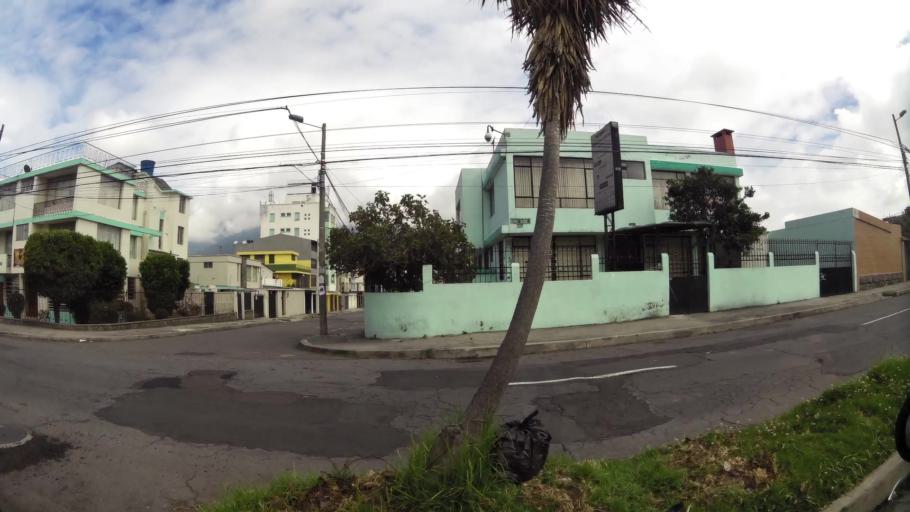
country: EC
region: Pichincha
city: Quito
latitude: -0.1649
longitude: -78.4767
